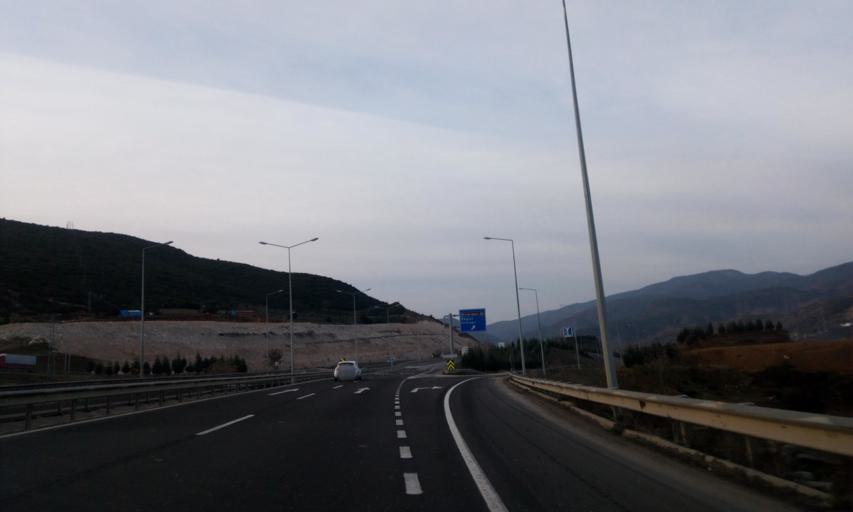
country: TR
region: Bilecik
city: Kuplu
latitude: 40.1230
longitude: 30.0134
